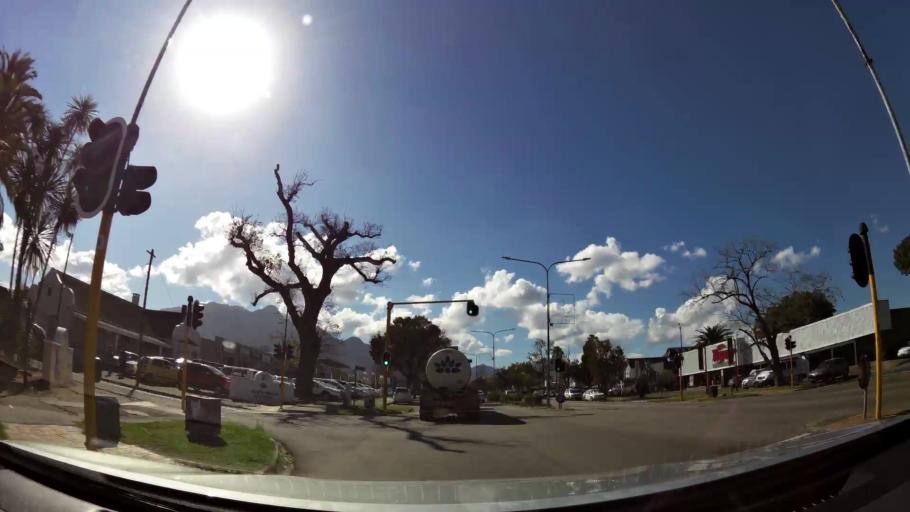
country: ZA
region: Western Cape
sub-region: Eden District Municipality
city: George
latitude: -33.9669
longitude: 22.4503
